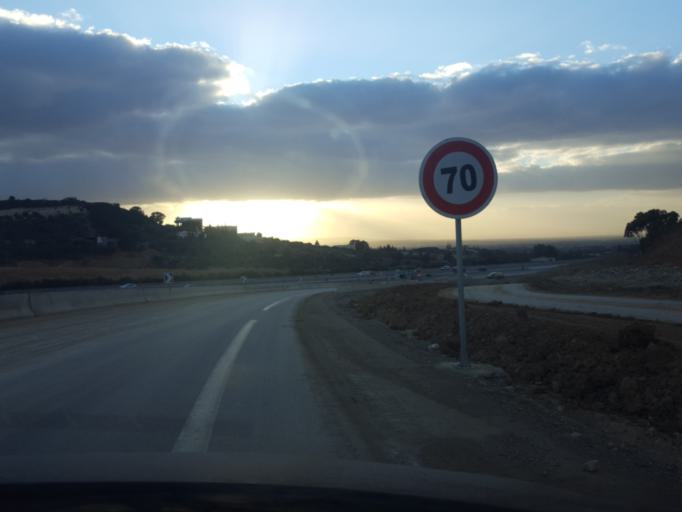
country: TN
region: Tunis
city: La Sebala du Mornag
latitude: 36.6472
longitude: 10.3651
